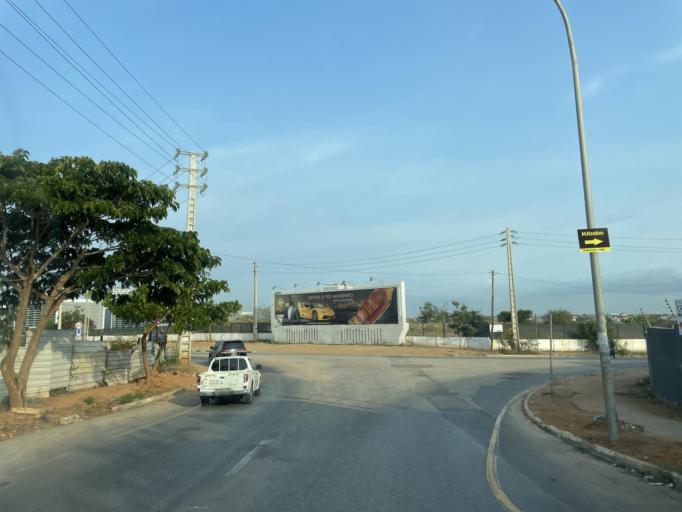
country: AO
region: Luanda
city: Luanda
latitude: -8.9187
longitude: 13.1969
